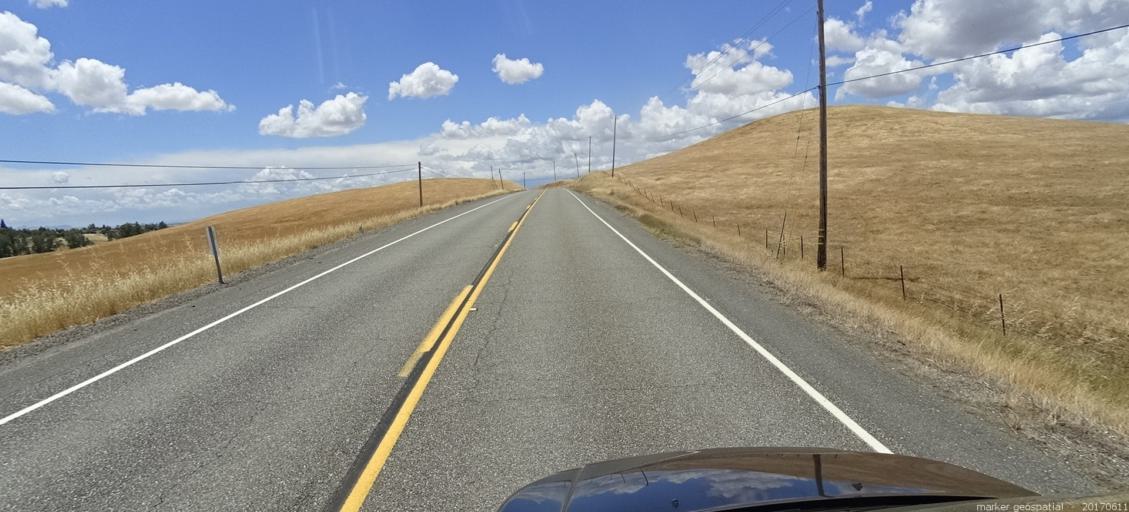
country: US
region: California
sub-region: Butte County
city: Paradise
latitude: 39.6513
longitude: -121.5988
